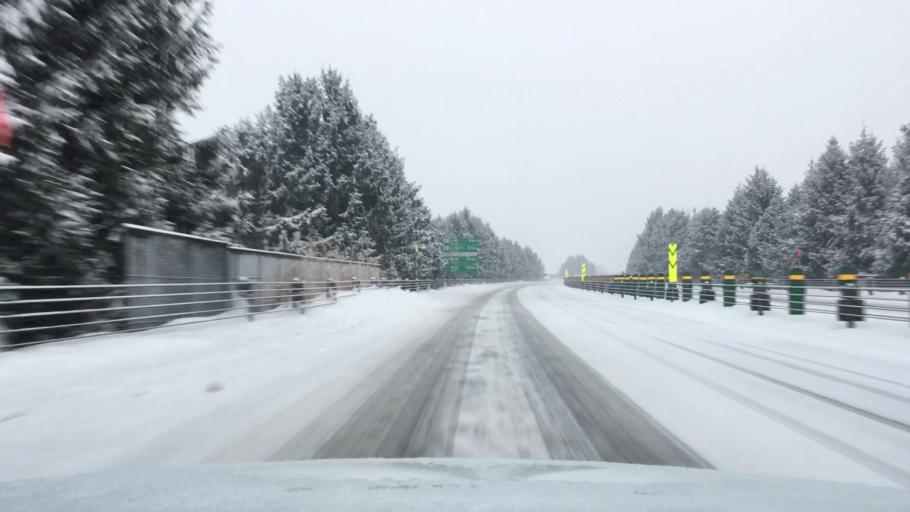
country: JP
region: Akita
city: Hanawa
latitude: 40.2696
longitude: 140.7634
